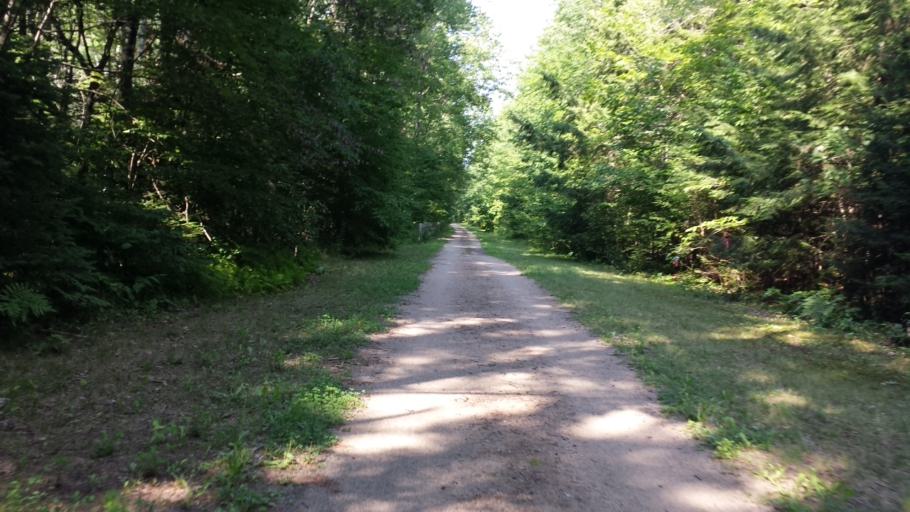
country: US
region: Maine
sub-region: York County
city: Kennebunk
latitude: 43.4386
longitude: -70.5258
